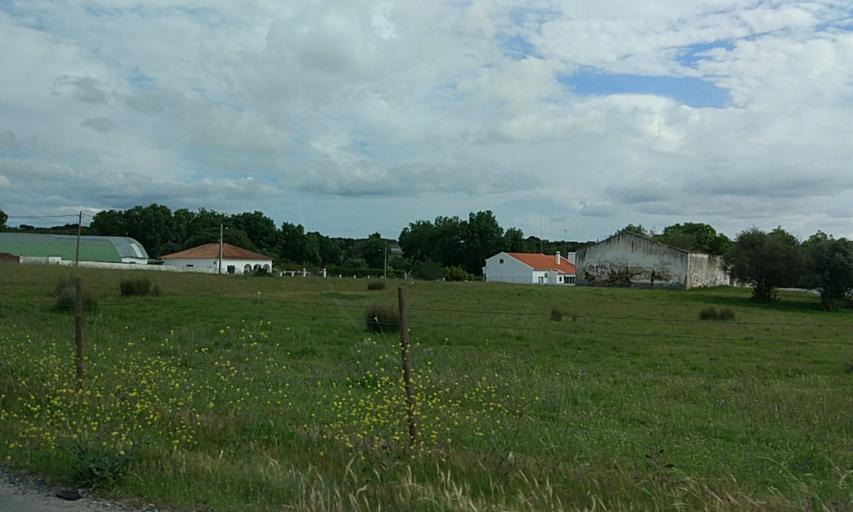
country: PT
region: Evora
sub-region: Evora
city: Evora
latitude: 38.5677
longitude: -7.9492
